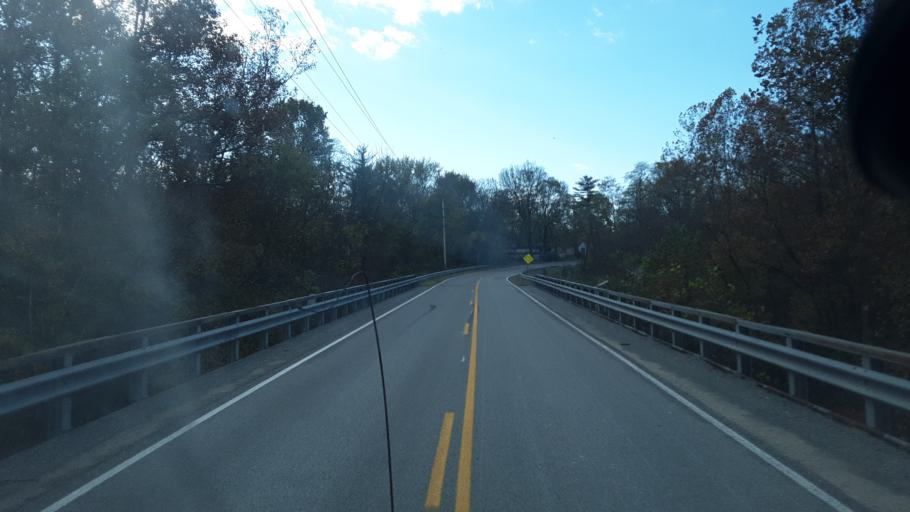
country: US
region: Ohio
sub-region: Highland County
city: Leesburg
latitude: 39.3292
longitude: -83.4741
